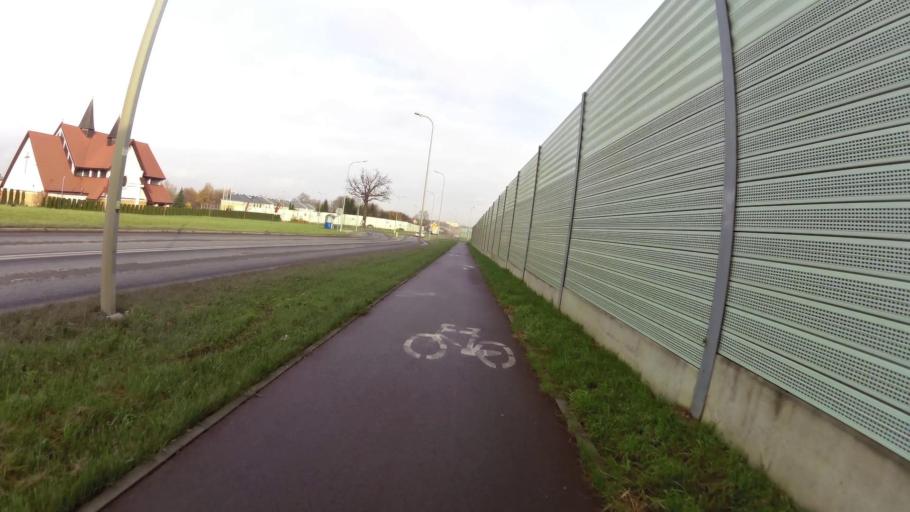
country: PL
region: West Pomeranian Voivodeship
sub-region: Koszalin
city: Koszalin
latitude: 54.2071
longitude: 16.1587
